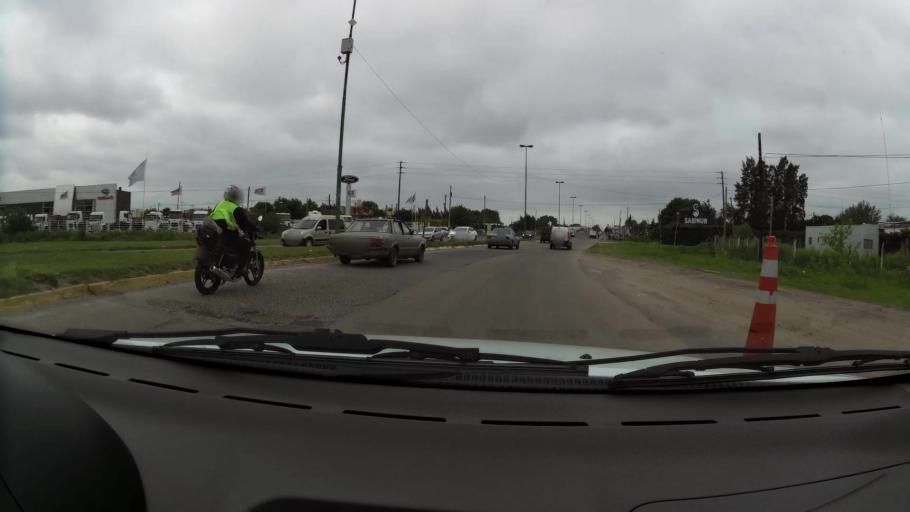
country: AR
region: Buenos Aires
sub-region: Partido de La Plata
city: La Plata
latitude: -34.9893
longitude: -58.0414
